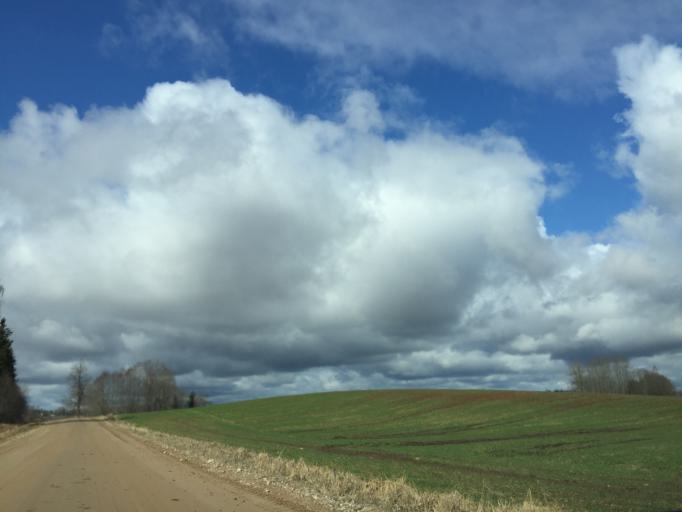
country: LV
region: Akniste
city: Akniste
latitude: 56.0960
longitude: 25.9833
